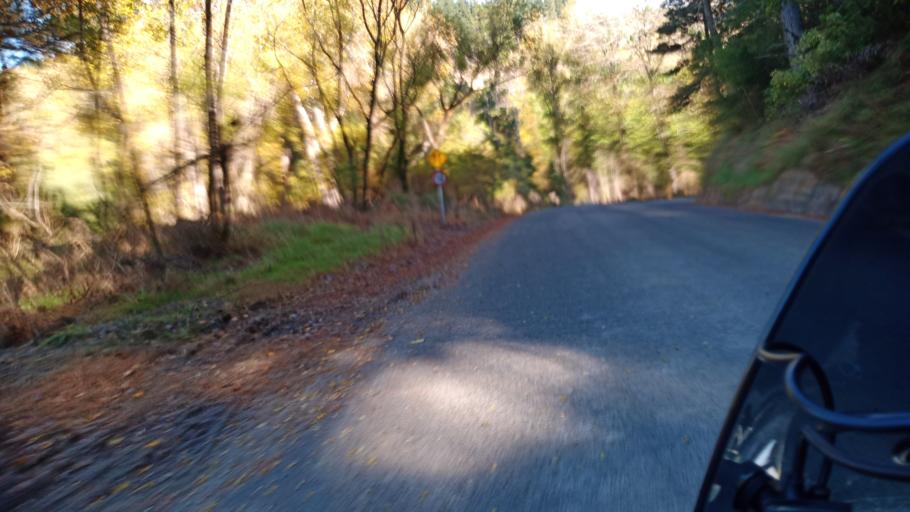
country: NZ
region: Hawke's Bay
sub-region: Wairoa District
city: Wairoa
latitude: -38.9203
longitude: 177.2420
